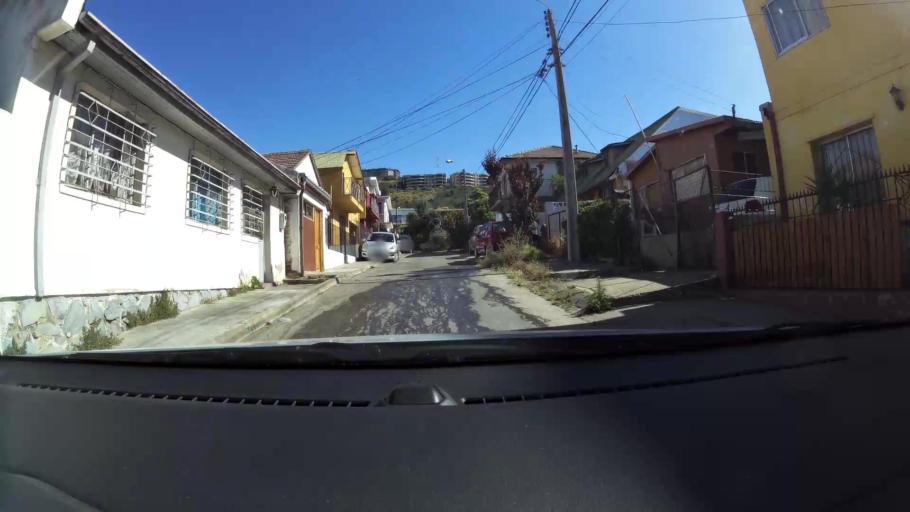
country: CL
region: Valparaiso
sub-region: Provincia de Valparaiso
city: Vina del Mar
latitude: -33.0326
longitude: -71.5681
